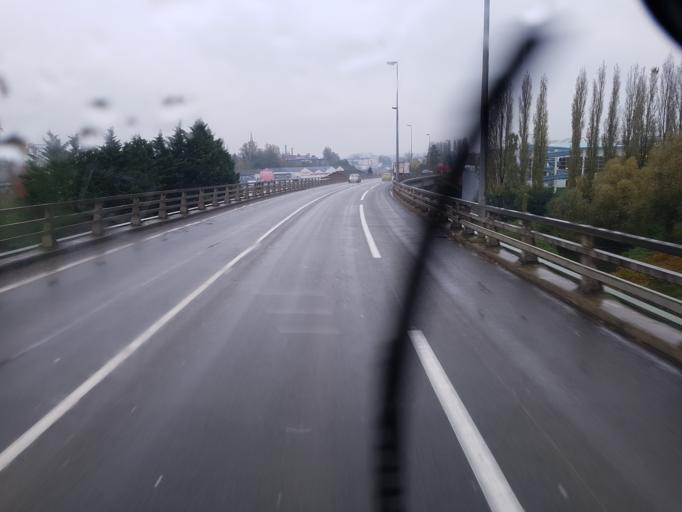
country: FR
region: Picardie
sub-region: Departement de l'Aisne
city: Saint-Quentin
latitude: 49.8366
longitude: 3.2857
